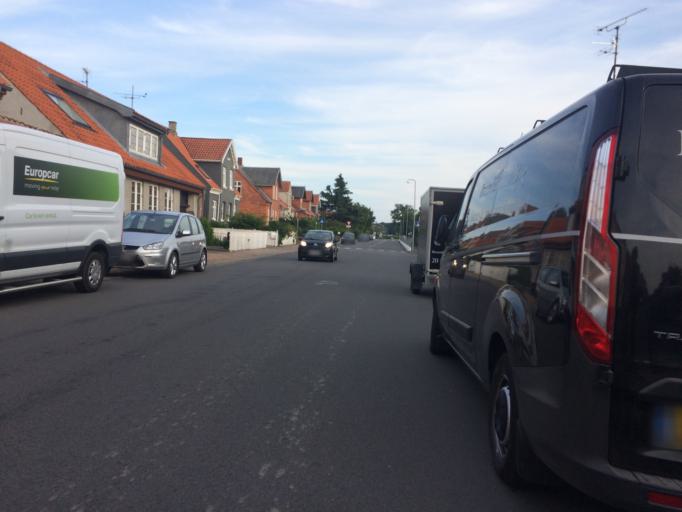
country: DK
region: Capital Region
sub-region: Bornholm Kommune
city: Ronne
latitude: 55.0969
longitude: 14.7021
